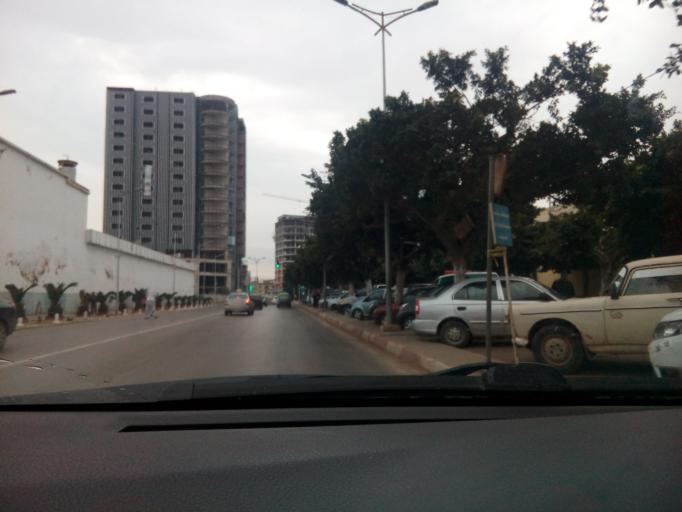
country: DZ
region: Oran
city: Oran
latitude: 35.6912
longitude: -0.6444
